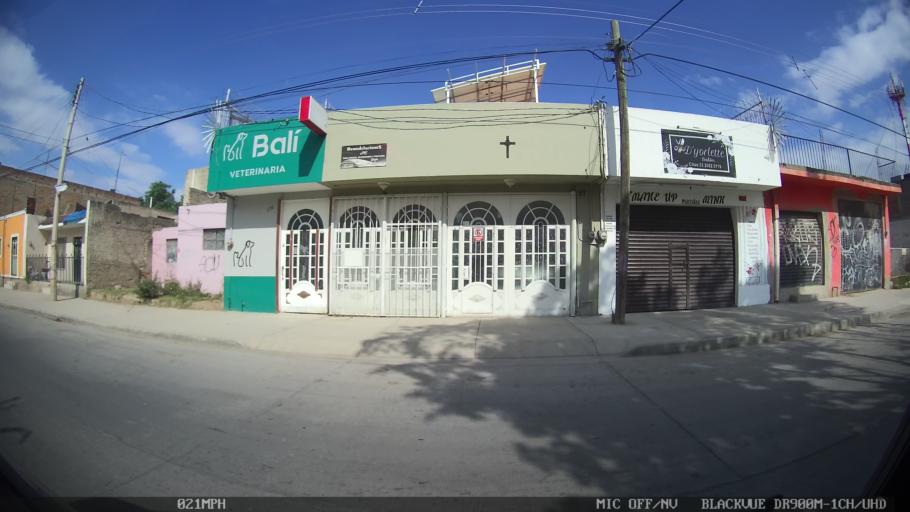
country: MX
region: Jalisco
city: Tonala
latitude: 20.6548
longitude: -103.2513
